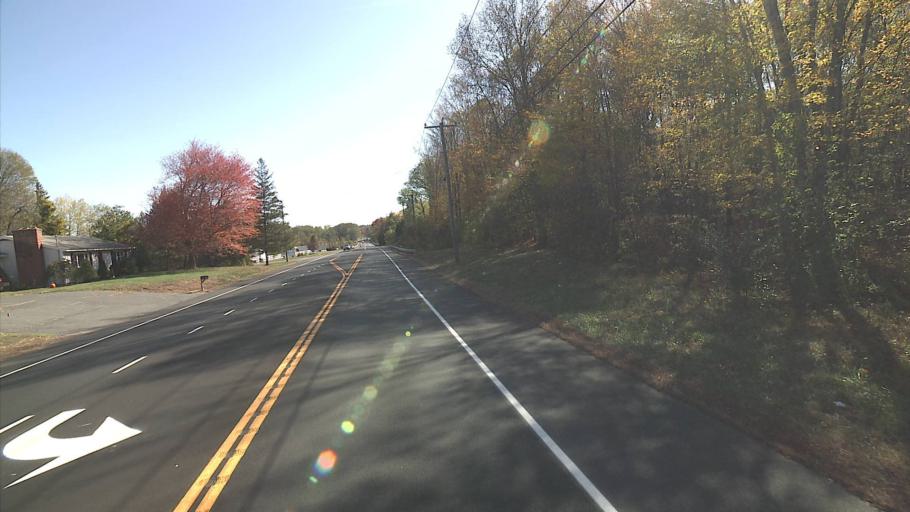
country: US
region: Connecticut
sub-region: Tolland County
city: South Coventry
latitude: 41.7284
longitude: -72.3205
